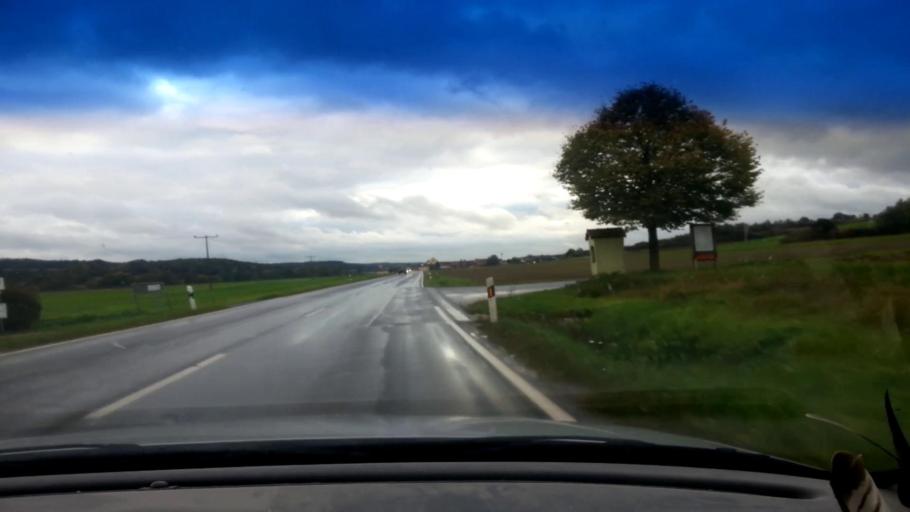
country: DE
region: Bavaria
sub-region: Upper Franconia
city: Burgwindheim
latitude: 49.8201
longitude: 10.6652
